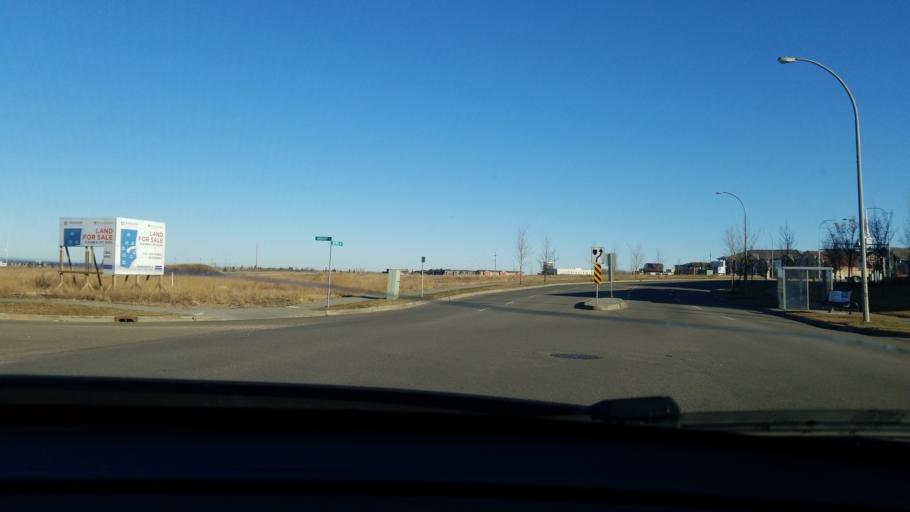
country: CA
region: Alberta
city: Sherwood Park
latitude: 53.5449
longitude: -113.3044
